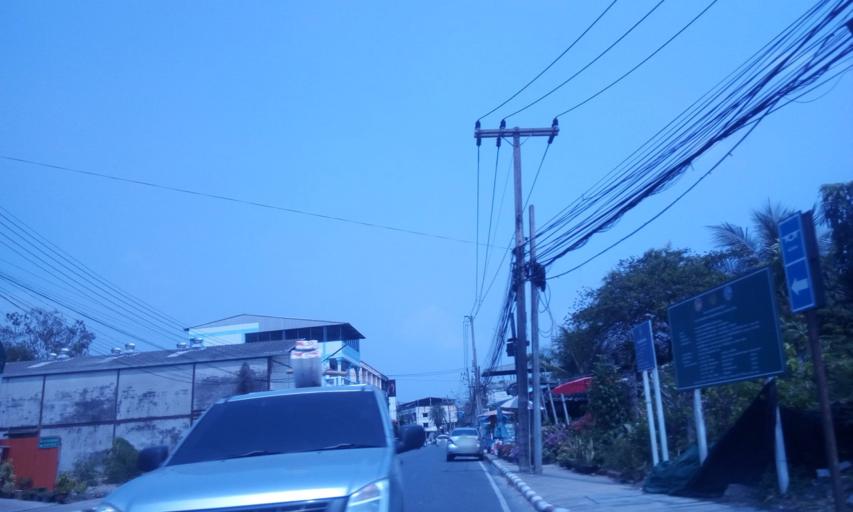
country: TH
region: Chon Buri
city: Phanat Nikhom
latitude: 13.4421
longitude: 101.1781
